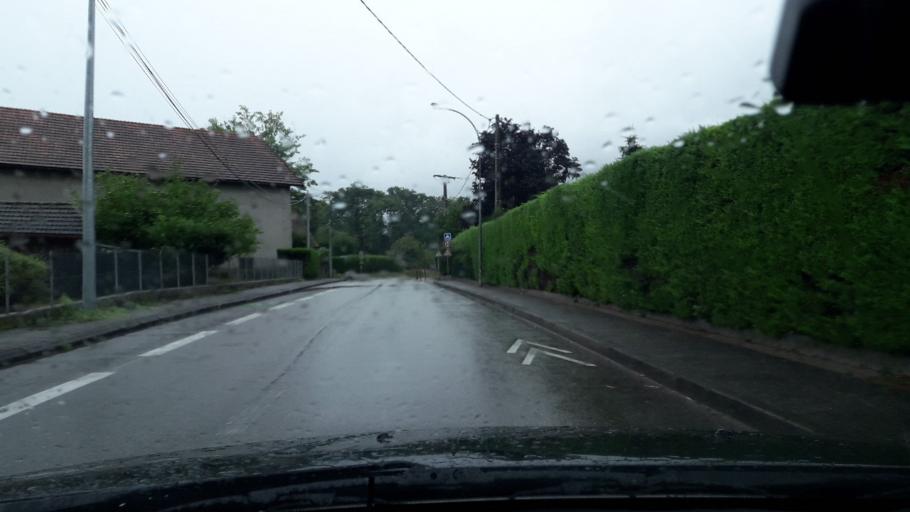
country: FR
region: Rhone-Alpes
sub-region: Departement de la Savoie
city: La Ravoire
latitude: 45.5531
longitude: 5.9643
